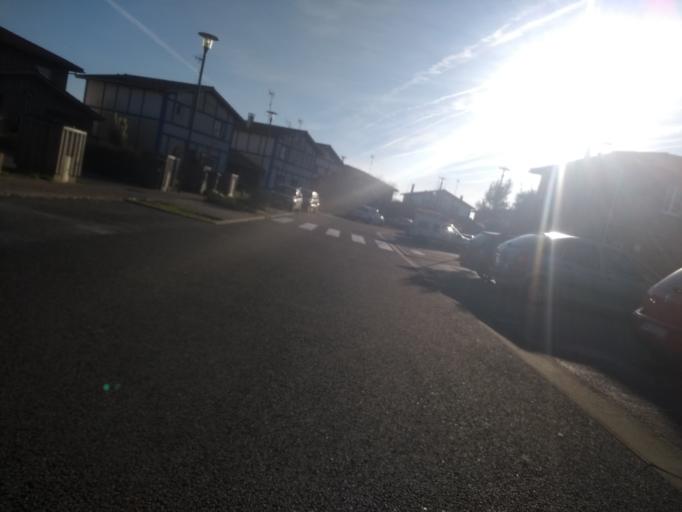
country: FR
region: Aquitaine
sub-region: Departement de la Gironde
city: Le Barp
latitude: 44.6082
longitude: -0.7822
